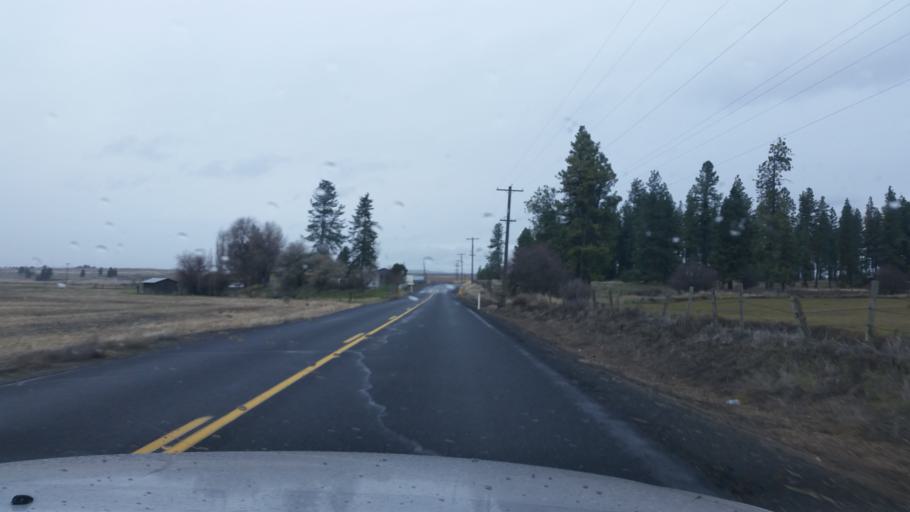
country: US
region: Washington
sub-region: Spokane County
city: Medical Lake
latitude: 47.6111
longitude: -117.7368
